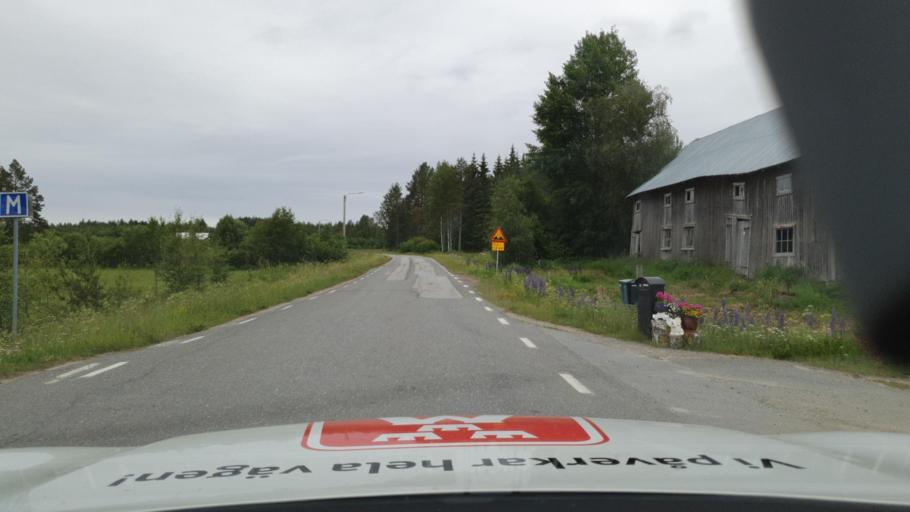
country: SE
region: Vaesterbotten
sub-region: Nordmalings Kommun
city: Nordmaling
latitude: 63.5034
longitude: 19.4172
